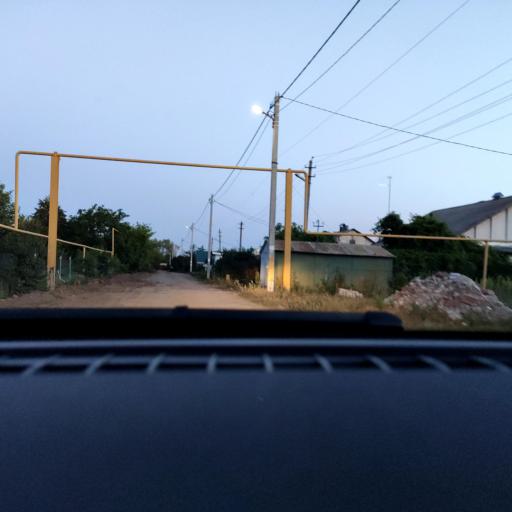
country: RU
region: Voronezj
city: Ramon'
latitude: 51.9294
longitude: 39.2520
